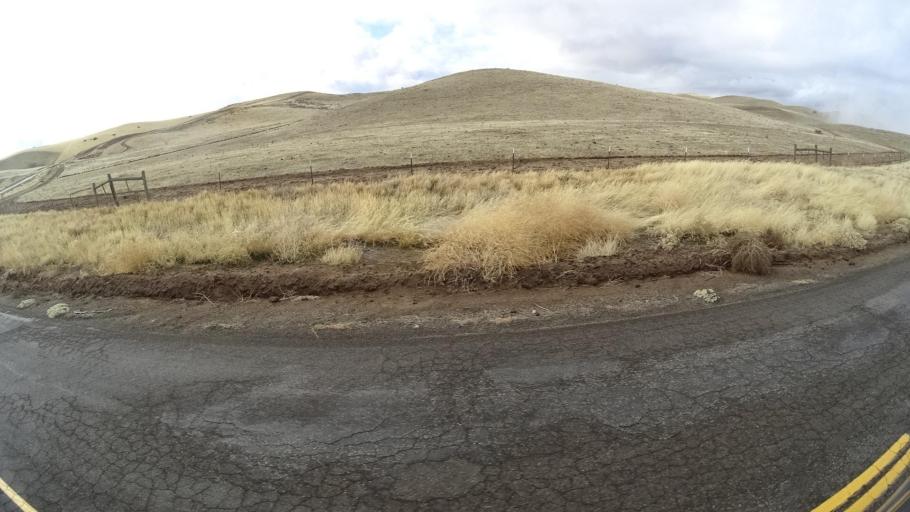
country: US
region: California
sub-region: Kern County
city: Maricopa
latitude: 34.9264
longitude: -119.4104
